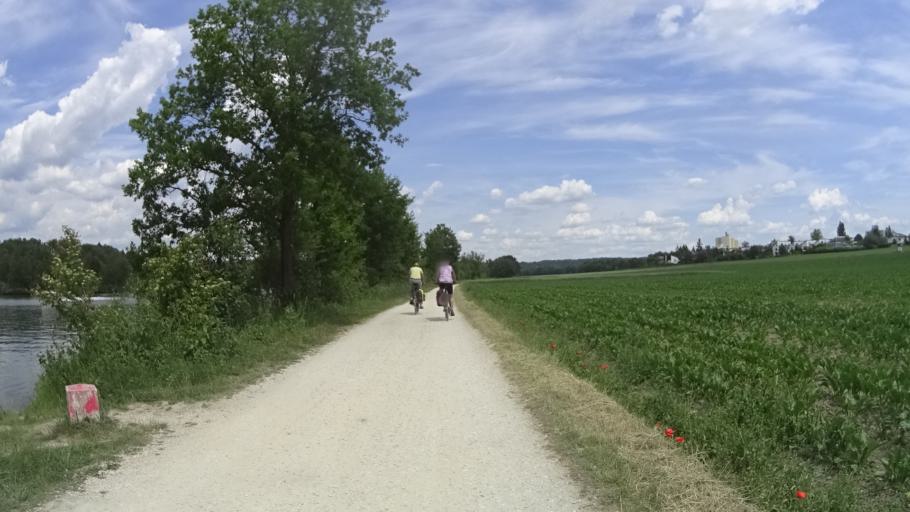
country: DE
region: Bavaria
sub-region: Upper Palatinate
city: Sinzing
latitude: 49.0157
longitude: 12.0334
